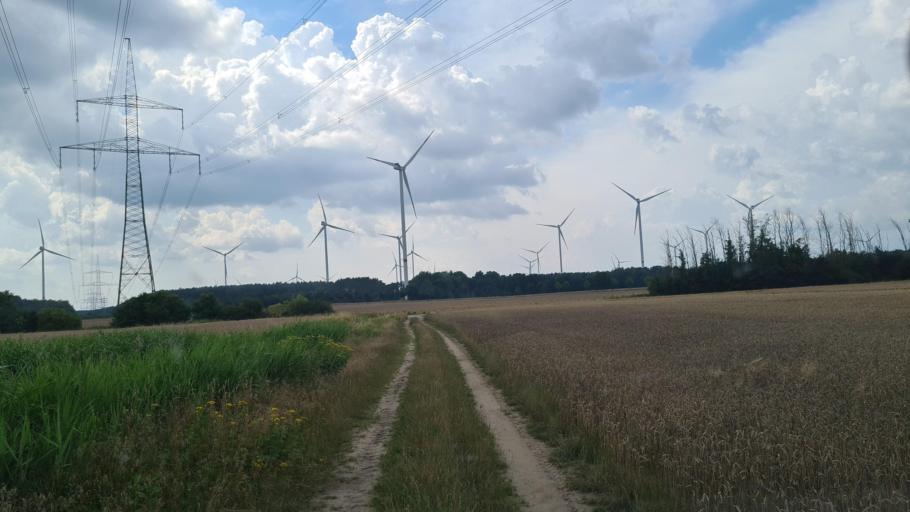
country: DE
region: Brandenburg
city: Sallgast
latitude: 51.6276
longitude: 13.8489
